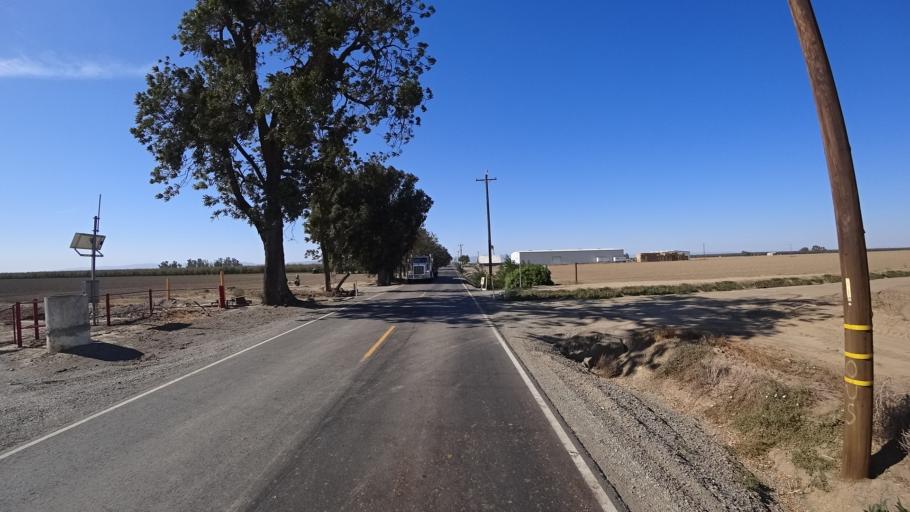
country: US
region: California
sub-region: Yolo County
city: Woodland
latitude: 38.6197
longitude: -121.8119
